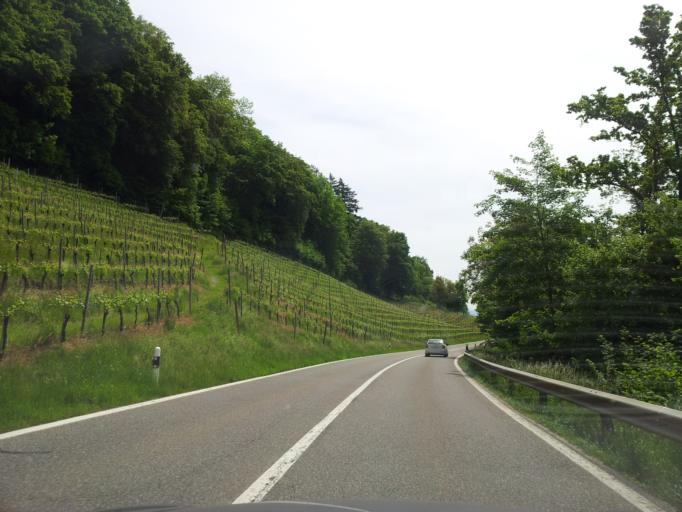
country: CH
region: Aargau
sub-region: Bezirk Baden
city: Wurenlos
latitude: 47.4365
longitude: 8.3724
